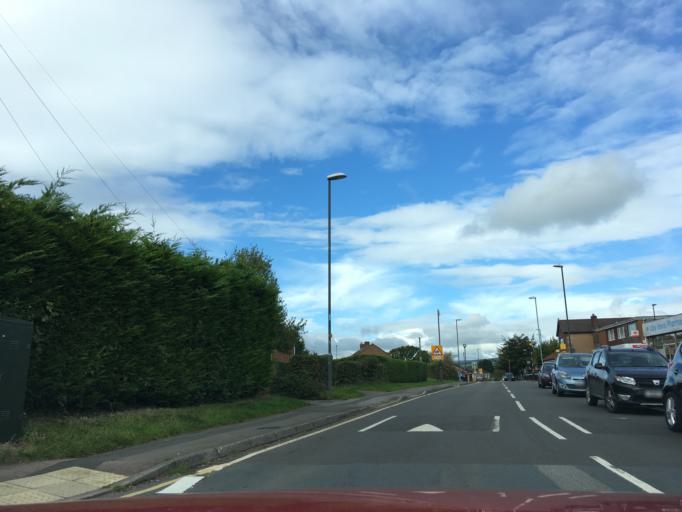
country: GB
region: Wales
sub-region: Monmouthshire
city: Chepstow
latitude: 51.6394
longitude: -2.6575
